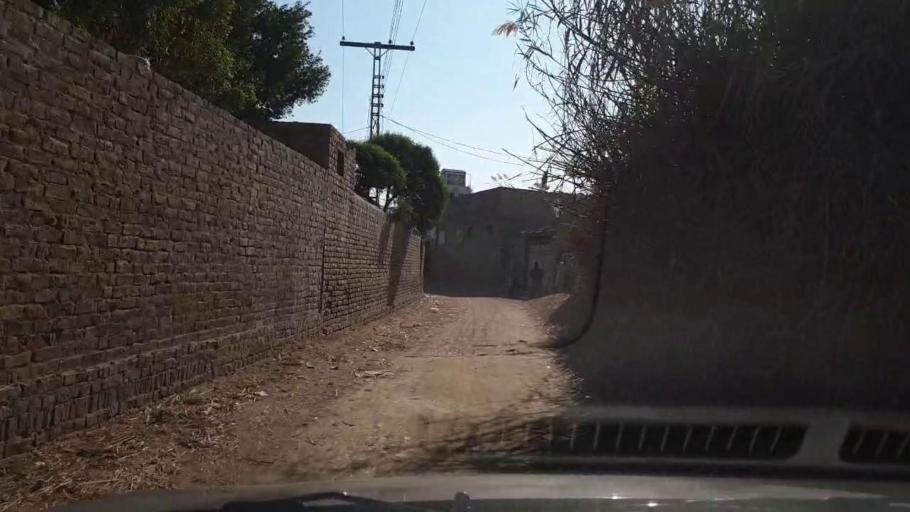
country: PK
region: Sindh
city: Jhol
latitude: 25.9327
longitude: 68.8279
